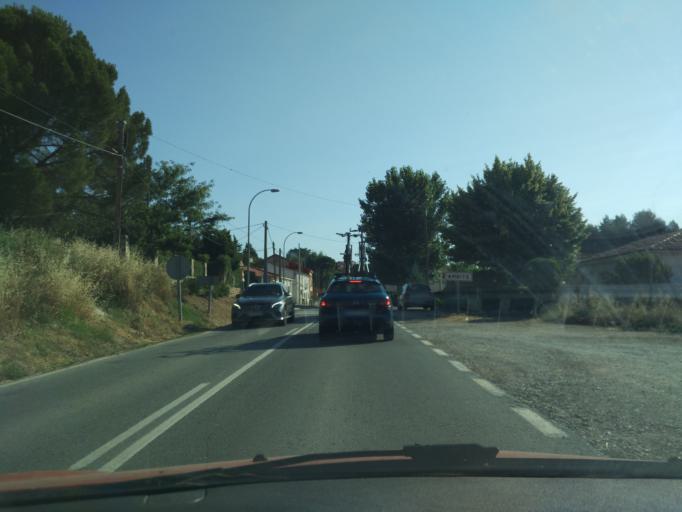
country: ES
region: Madrid
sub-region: Provincia de Madrid
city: Ambite
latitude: 40.3255
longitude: -3.1845
